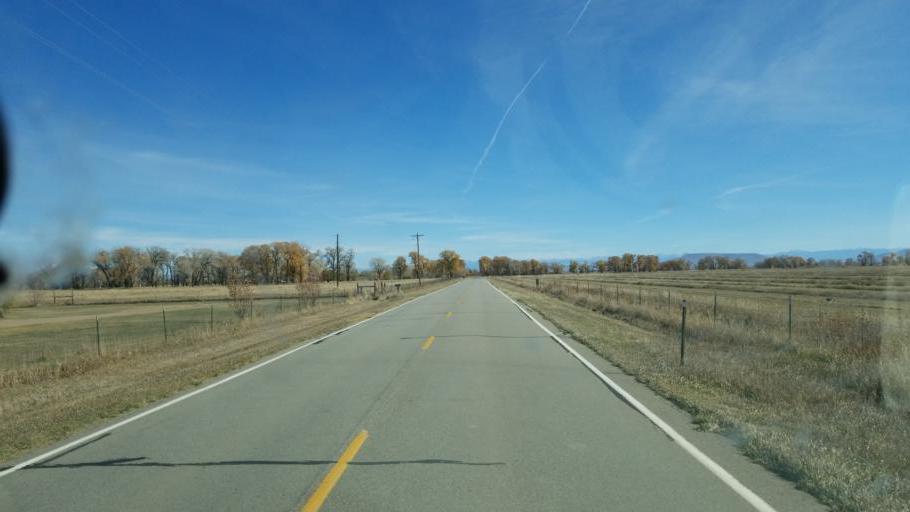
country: US
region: Colorado
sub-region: Conejos County
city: Conejos
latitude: 37.2836
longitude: -106.0893
